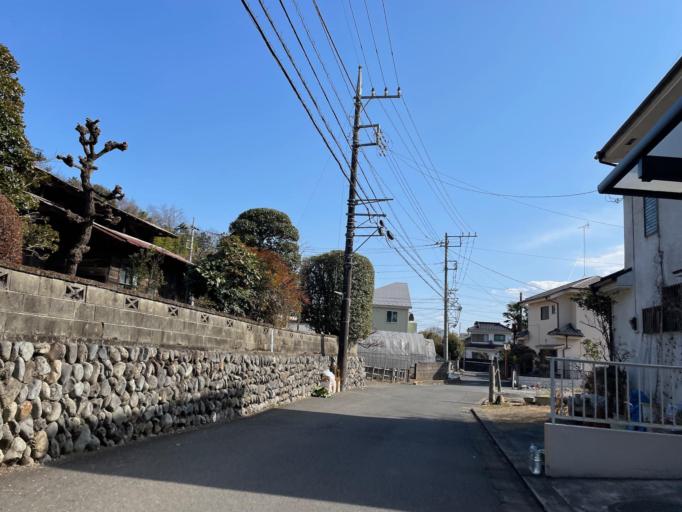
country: JP
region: Tokyo
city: Higashimurayama-shi
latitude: 35.7588
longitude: 139.3973
